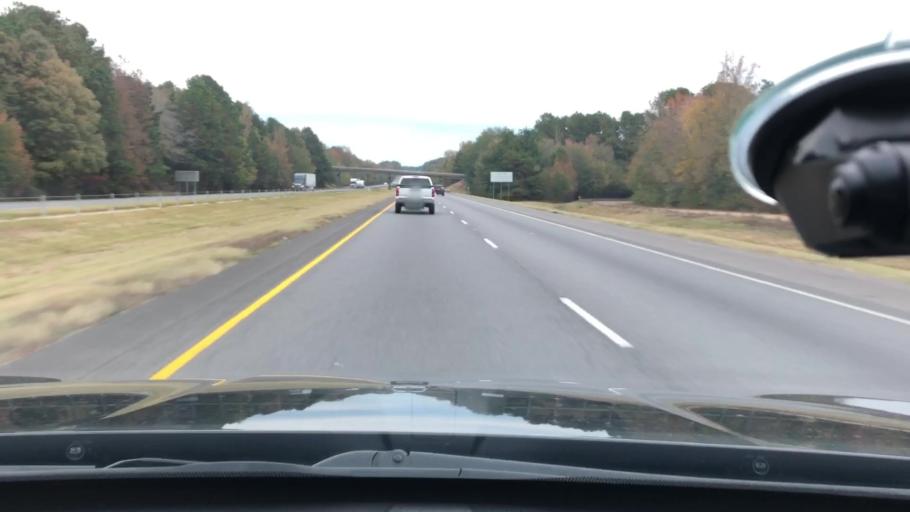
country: US
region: Arkansas
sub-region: Clark County
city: Gurdon
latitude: 34.0196
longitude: -93.1603
